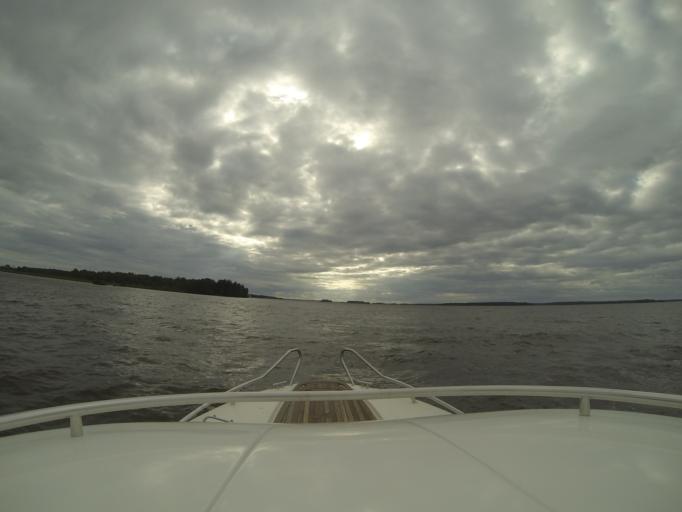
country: SE
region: Soedermanland
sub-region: Eskilstuna Kommun
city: Kvicksund
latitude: 59.4522
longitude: 16.2906
